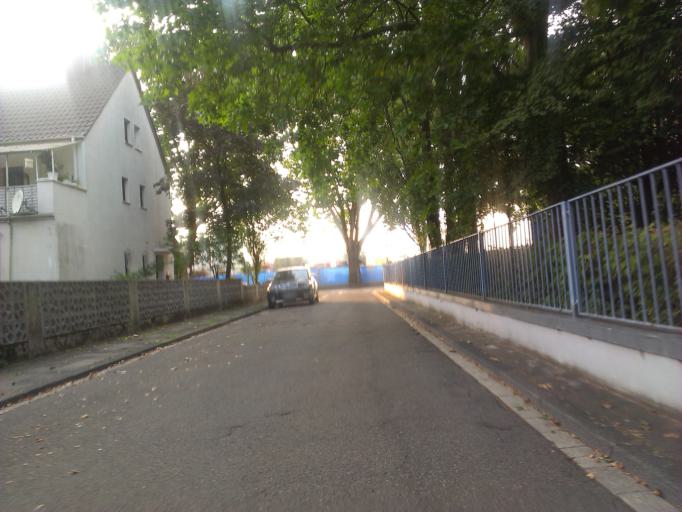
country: DE
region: Rheinland-Pfalz
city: Ludwigshafen am Rhein
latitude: 49.4658
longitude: 8.4520
